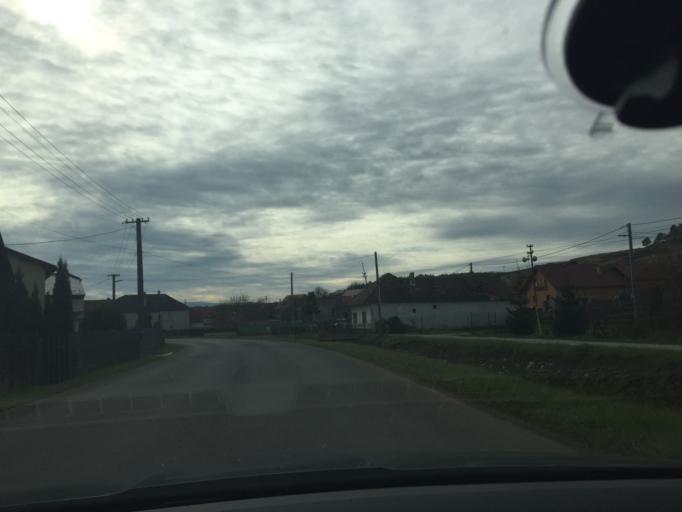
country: SK
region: Presovsky
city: Spisske Podhradie
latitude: 48.9804
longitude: 20.7917
